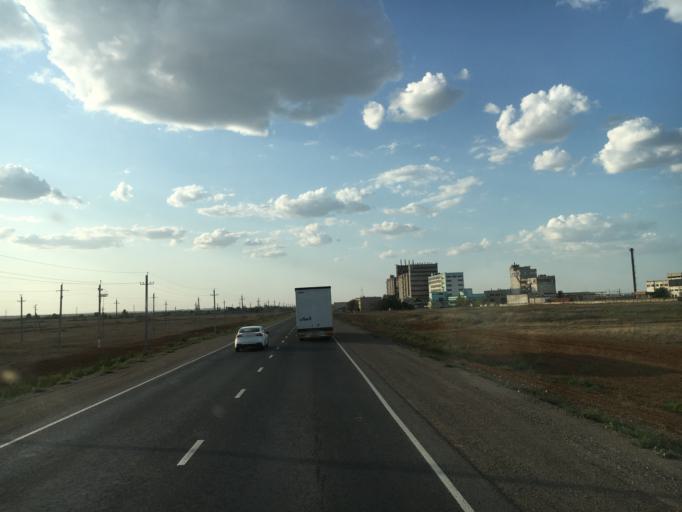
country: KZ
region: Aqtoebe
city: Aqtobe
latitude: 50.1866
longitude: 57.2382
